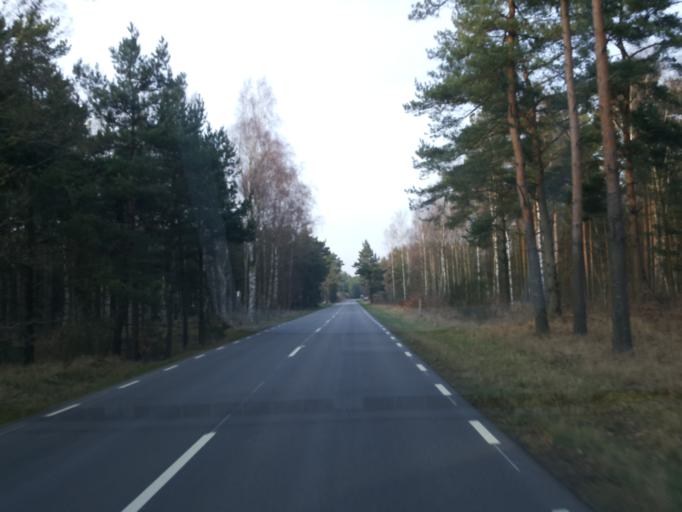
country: SE
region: Skane
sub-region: Simrishamns Kommun
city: Simrishamn
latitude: 55.4039
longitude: 14.1858
